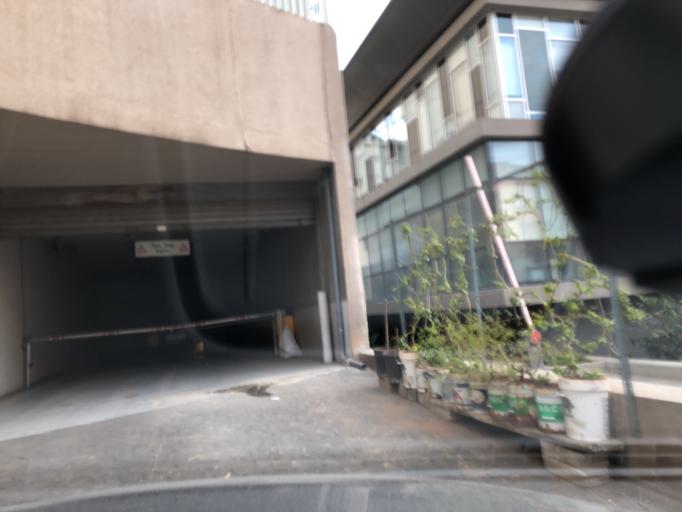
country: LB
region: Mont-Liban
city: Baabda
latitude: 33.8638
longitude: 35.5467
